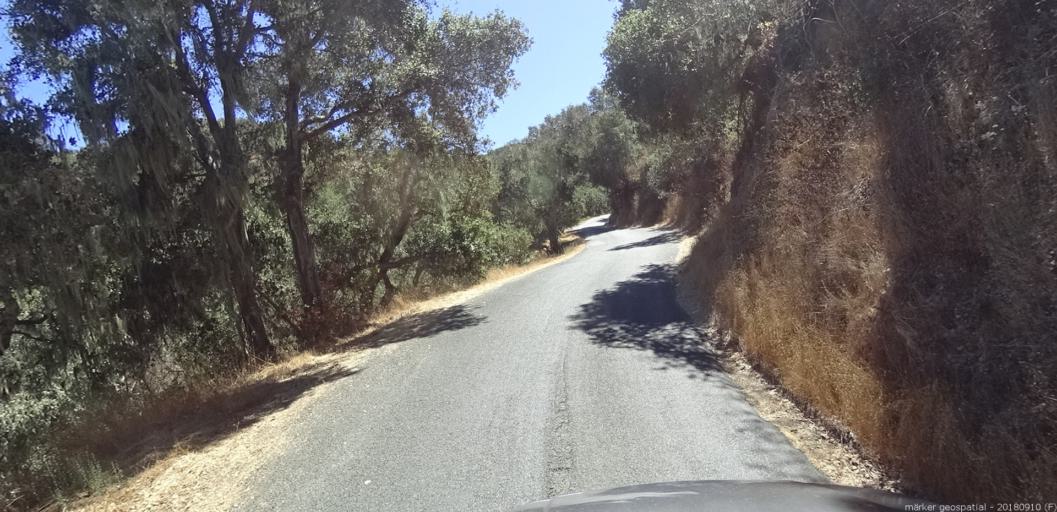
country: US
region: California
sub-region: Monterey County
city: Carmel Valley Village
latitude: 36.4850
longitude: -121.8058
